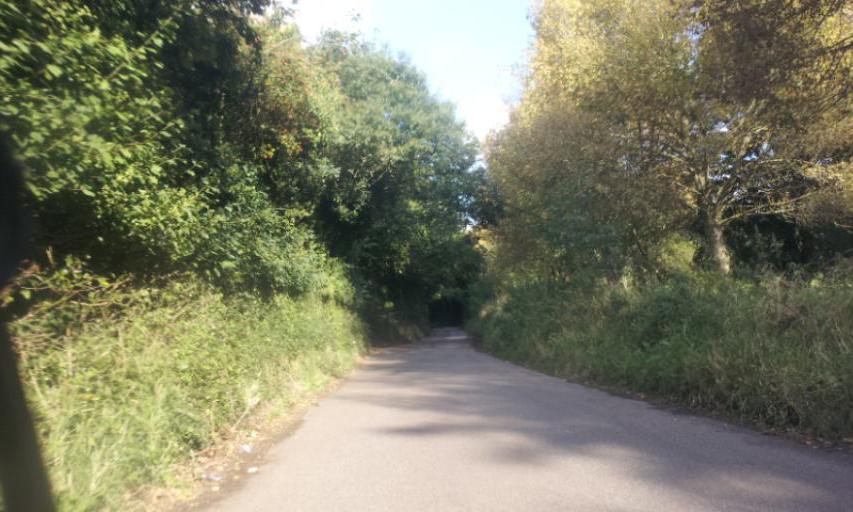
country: GB
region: England
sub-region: Kent
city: Swanley
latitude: 51.4066
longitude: 0.1722
